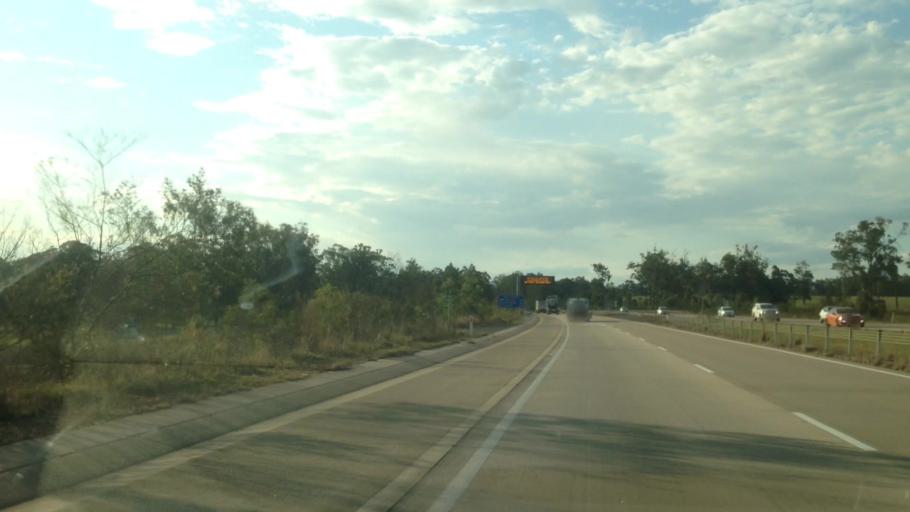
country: AU
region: New South Wales
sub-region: Cessnock
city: Heddon Greta
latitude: -32.8375
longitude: 151.5398
